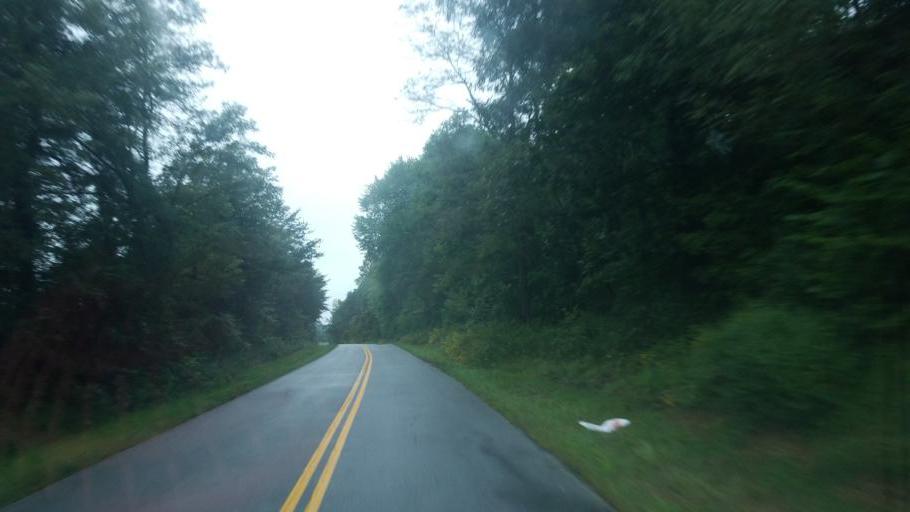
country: US
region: Kentucky
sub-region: Fleming County
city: Flemingsburg
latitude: 38.4057
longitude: -83.5958
